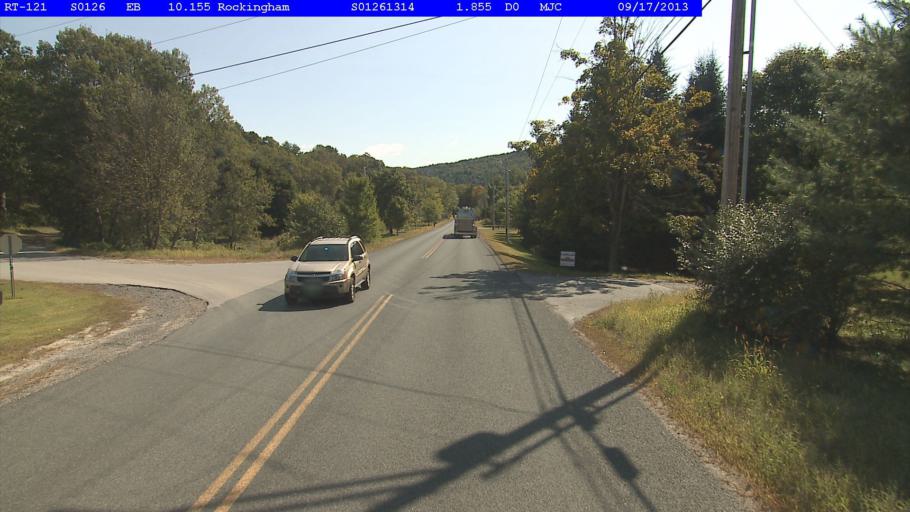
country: US
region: Vermont
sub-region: Windham County
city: Rockingham
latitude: 43.1375
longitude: -72.5278
